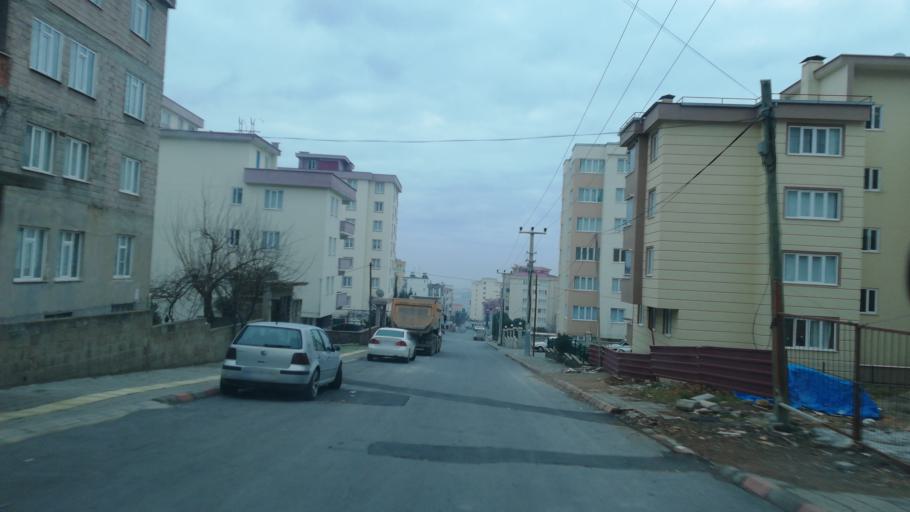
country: TR
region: Kahramanmaras
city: Kahramanmaras
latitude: 37.5970
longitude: 36.8986
